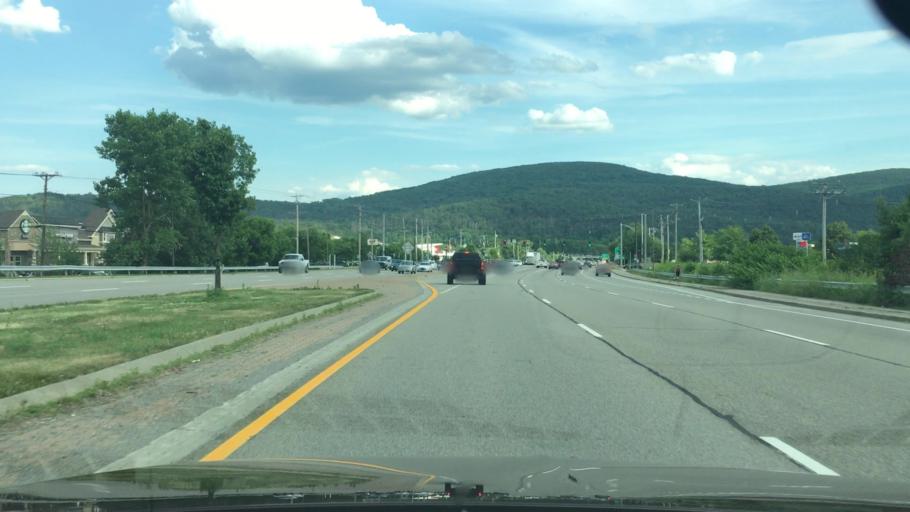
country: US
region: New York
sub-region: Dutchess County
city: Fishkill
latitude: 41.5314
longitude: -73.8948
